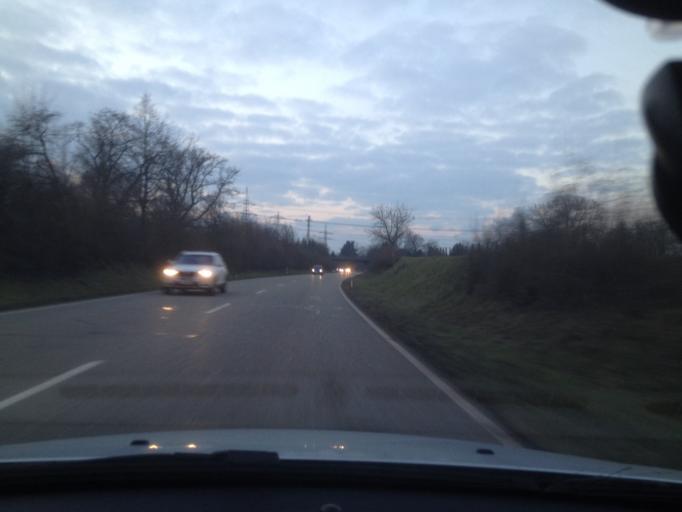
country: DE
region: Baden-Wuerttemberg
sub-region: Karlsruhe Region
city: Ettlingen
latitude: 48.9556
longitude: 8.4114
